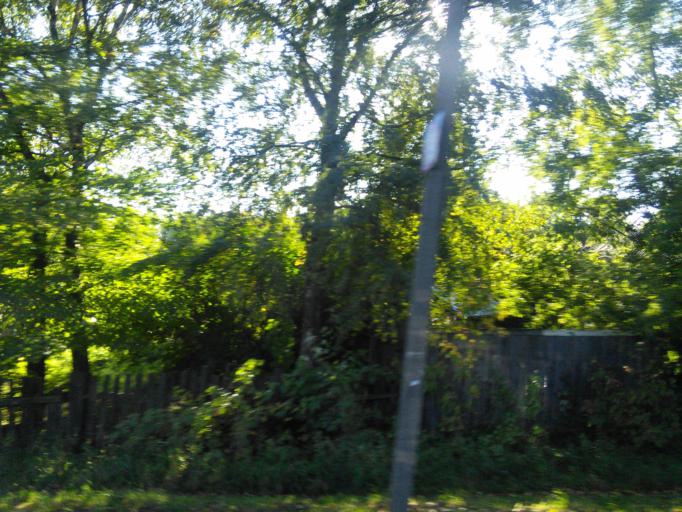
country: RU
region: Jaroslavl
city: Rybinsk
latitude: 58.0578
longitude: 38.8546
